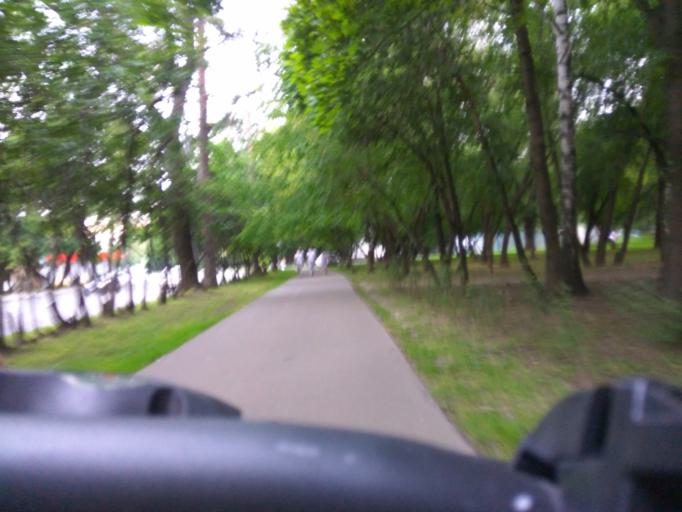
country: RU
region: Moscow
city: Tsaritsyno
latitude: 55.6235
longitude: 37.6558
